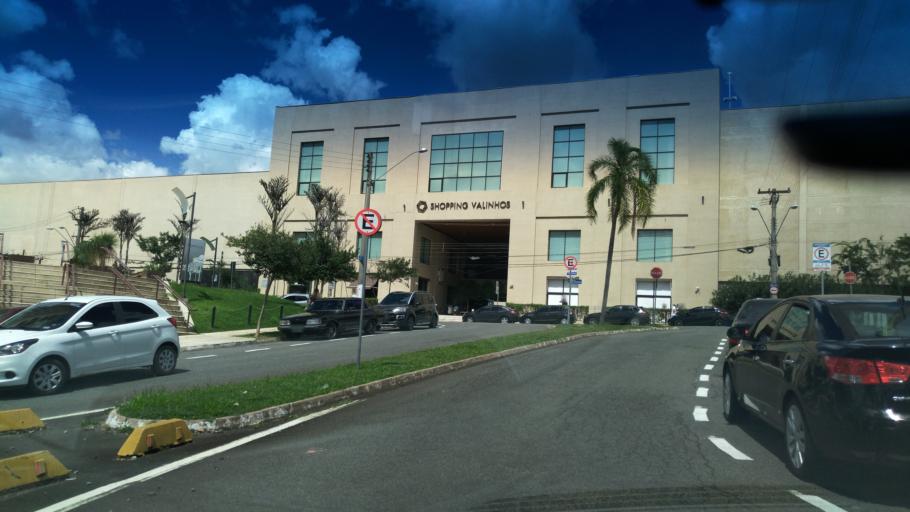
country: BR
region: Sao Paulo
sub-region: Valinhos
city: Valinhos
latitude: -22.9810
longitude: -47.0131
